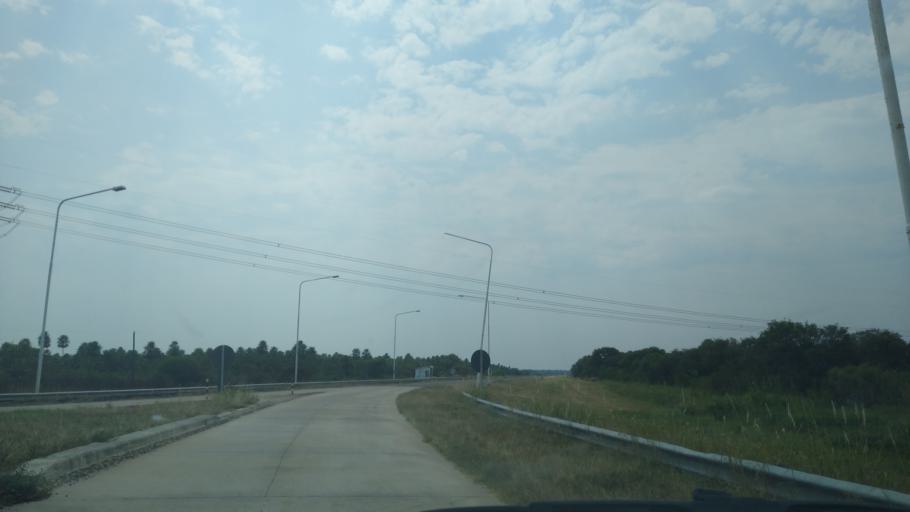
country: AR
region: Chaco
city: Margarita Belen
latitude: -27.0849
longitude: -58.9590
